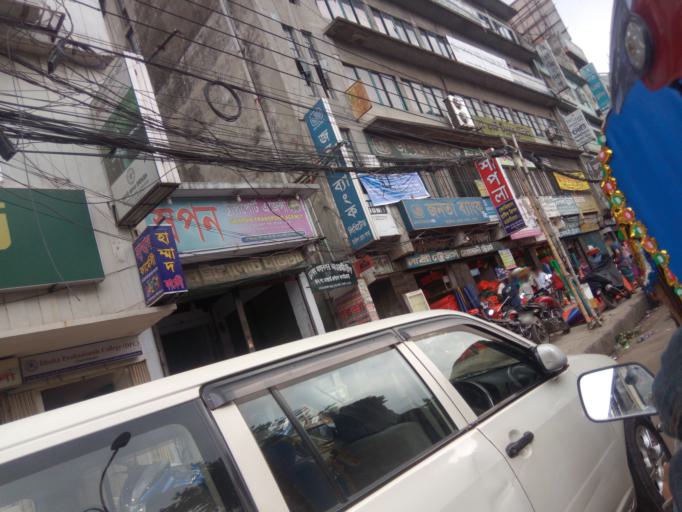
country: BD
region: Dhaka
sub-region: Dhaka
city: Dhaka
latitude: 23.7137
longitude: 90.4121
